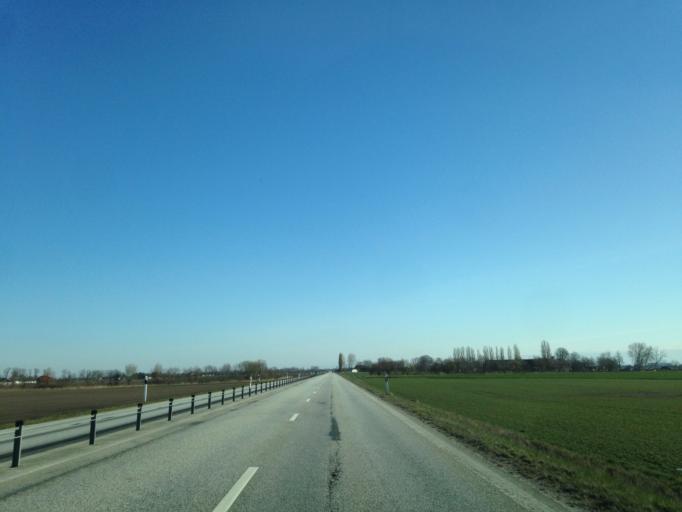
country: SE
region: Skane
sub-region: Vellinge Kommun
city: Vellinge
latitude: 55.4452
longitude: 12.9946
